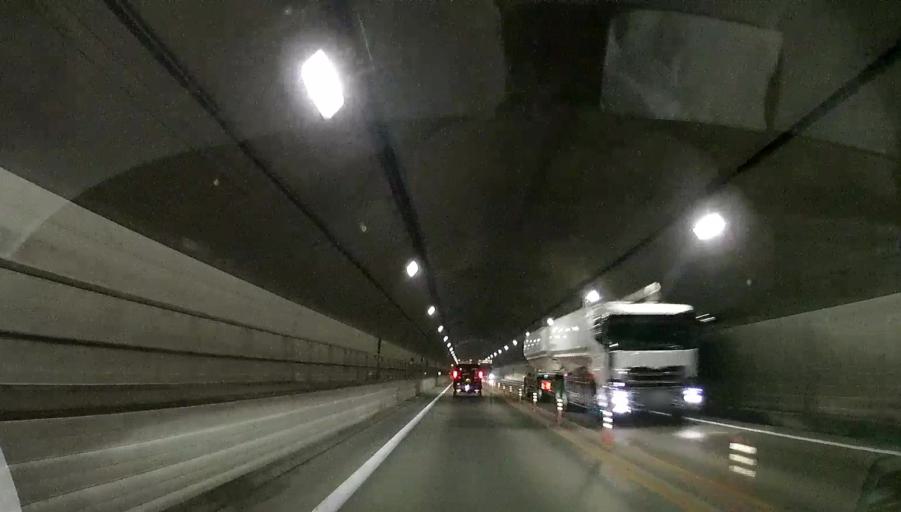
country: JP
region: Hokkaido
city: Shimo-furano
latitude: 43.0583
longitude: 142.5101
